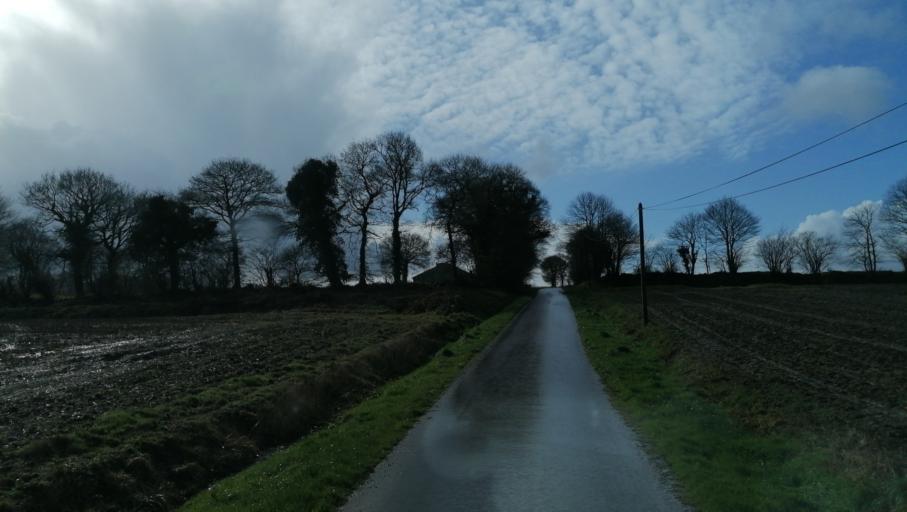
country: FR
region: Brittany
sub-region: Departement des Cotes-d'Armor
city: Lanrodec
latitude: 48.4900
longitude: -3.0264
